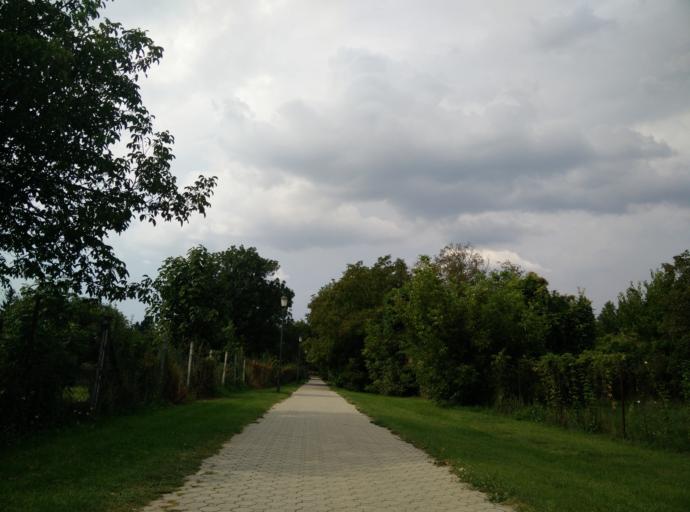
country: HU
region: Pest
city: Paty
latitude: 47.5130
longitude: 18.8291
